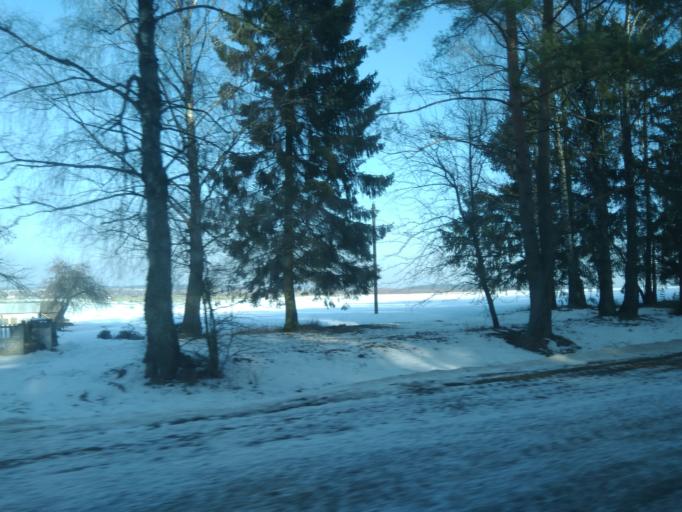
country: BY
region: Minsk
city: Snow
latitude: 53.2138
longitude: 26.4512
